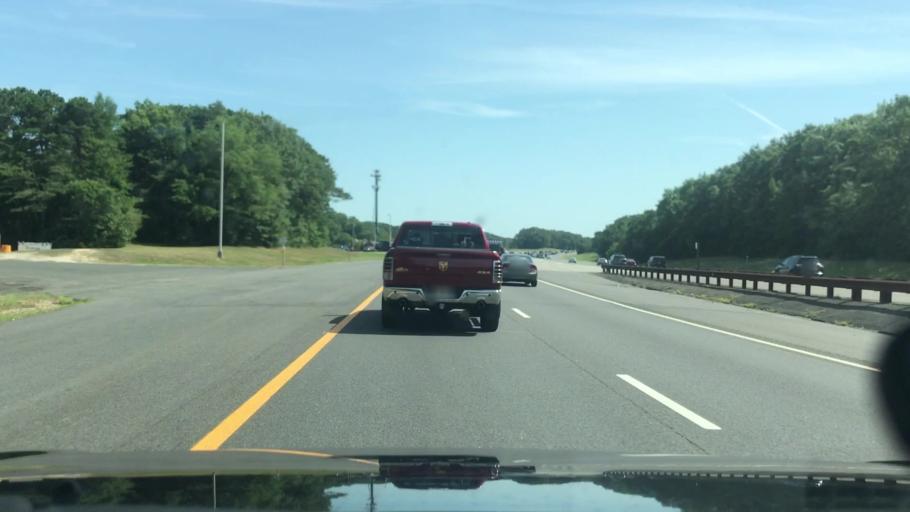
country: US
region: New Jersey
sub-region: Monmouth County
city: Eatontown
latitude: 40.2549
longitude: -74.0818
